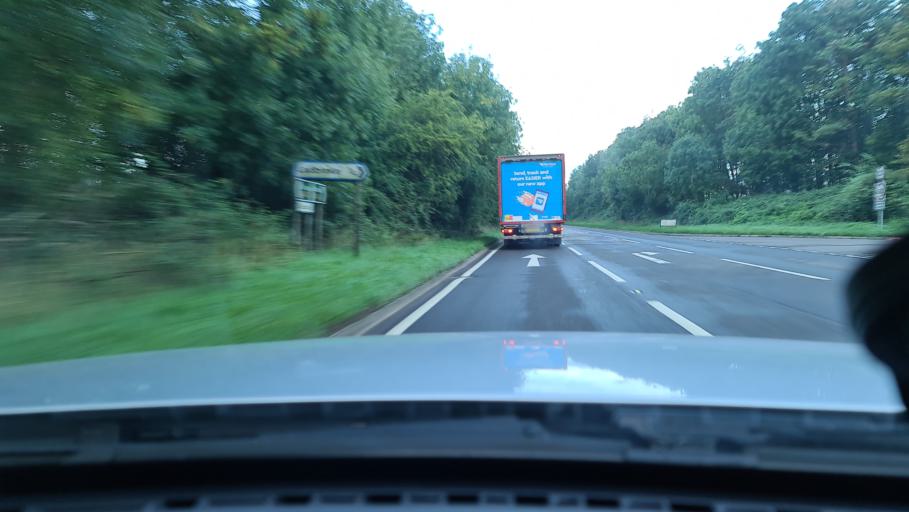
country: GB
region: England
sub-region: Warwickshire
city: Southam
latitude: 52.2232
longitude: -1.3879
